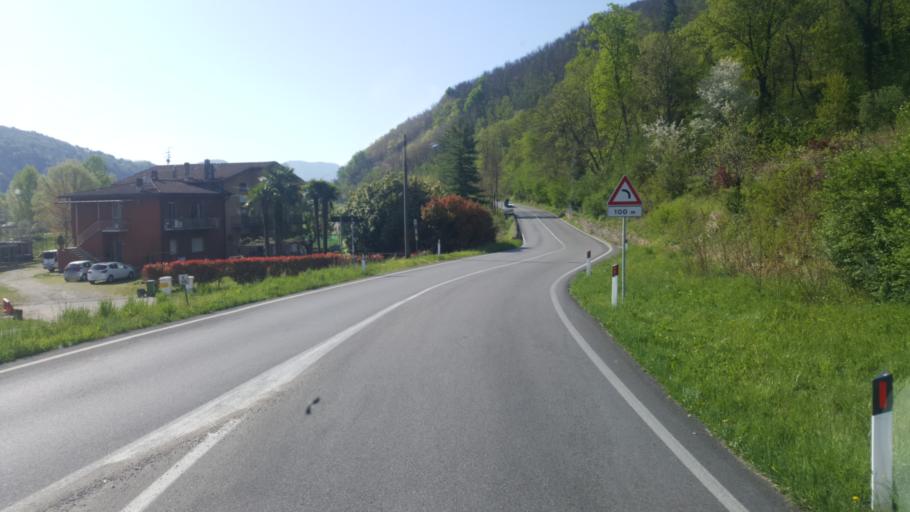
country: IT
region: Lombardy
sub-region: Provincia di Varese
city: Germignaga
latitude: 45.9811
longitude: 8.7414
